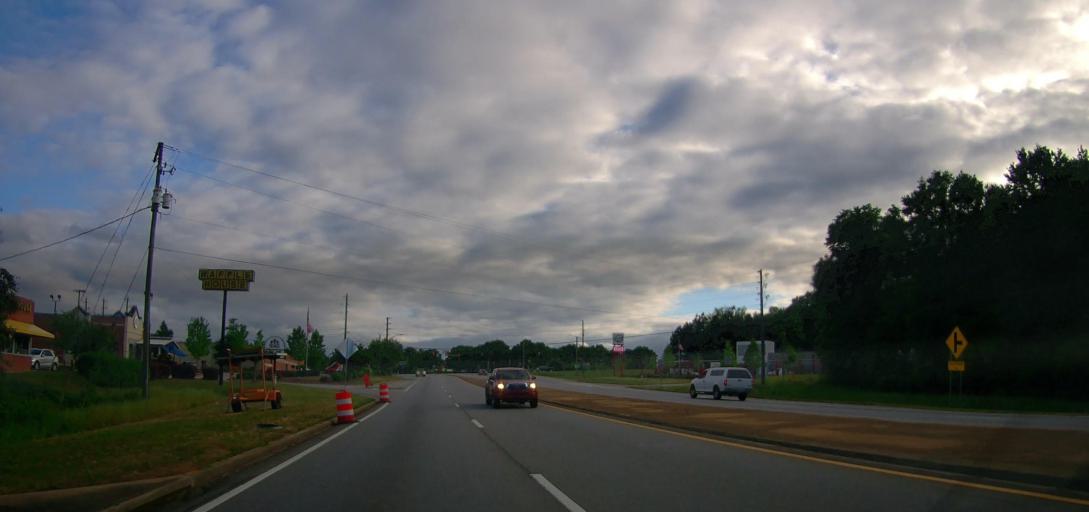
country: US
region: Georgia
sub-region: Oconee County
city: Watkinsville
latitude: 33.8903
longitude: -83.4129
